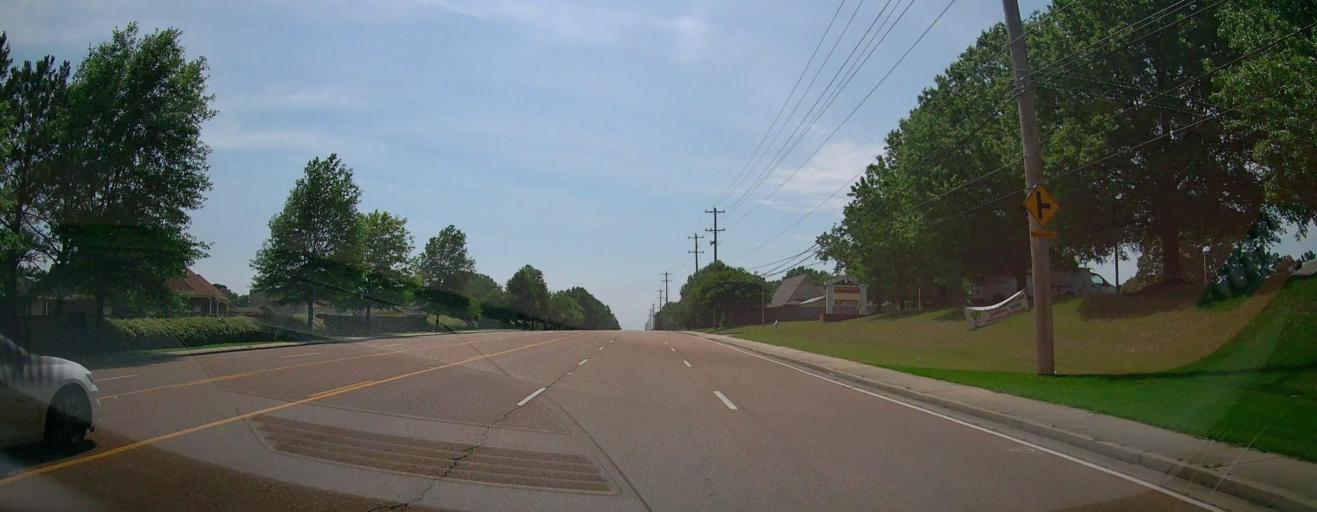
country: US
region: Mississippi
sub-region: De Soto County
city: Olive Branch
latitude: 35.0205
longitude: -89.8120
